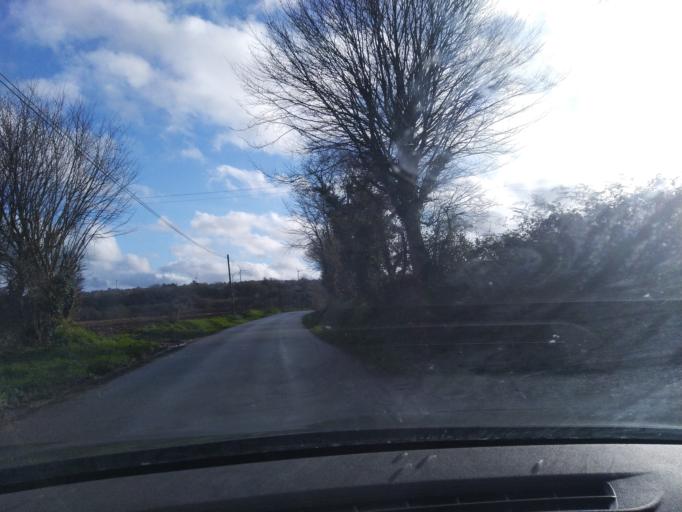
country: FR
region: Brittany
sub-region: Departement du Finistere
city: Guerlesquin
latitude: 48.4873
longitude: -3.5835
